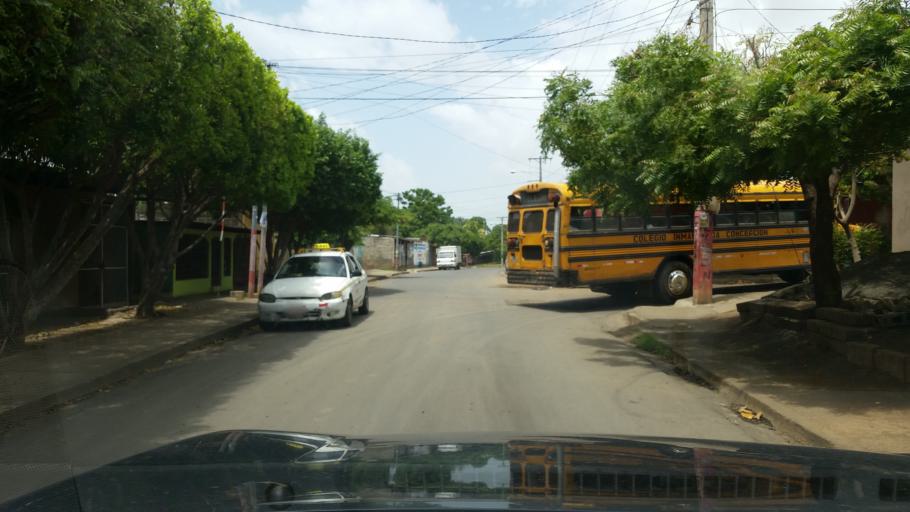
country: NI
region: Managua
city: Managua
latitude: 12.1199
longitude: -86.2210
